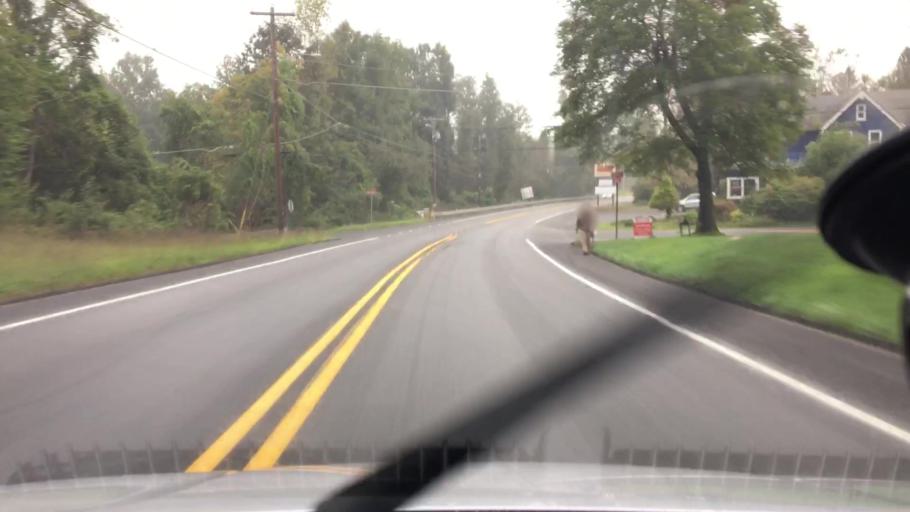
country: US
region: Pennsylvania
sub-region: Monroe County
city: Mount Pocono
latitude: 41.1285
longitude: -75.3159
